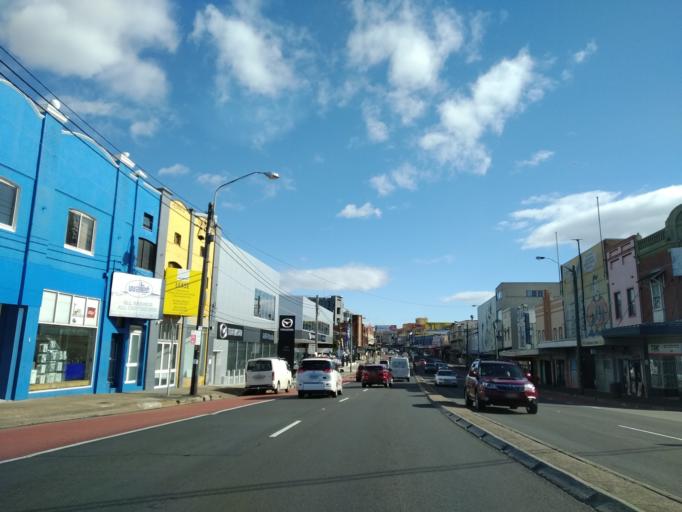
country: AU
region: New South Wales
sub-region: Leichhardt
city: Lilyfield
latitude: -33.8883
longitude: 151.1629
